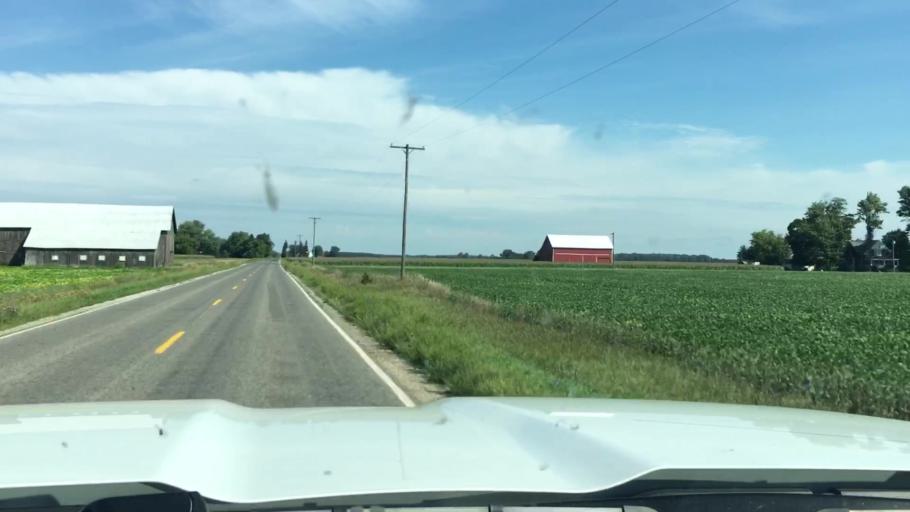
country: US
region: Michigan
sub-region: Saginaw County
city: Hemlock
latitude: 43.5089
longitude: -84.2296
